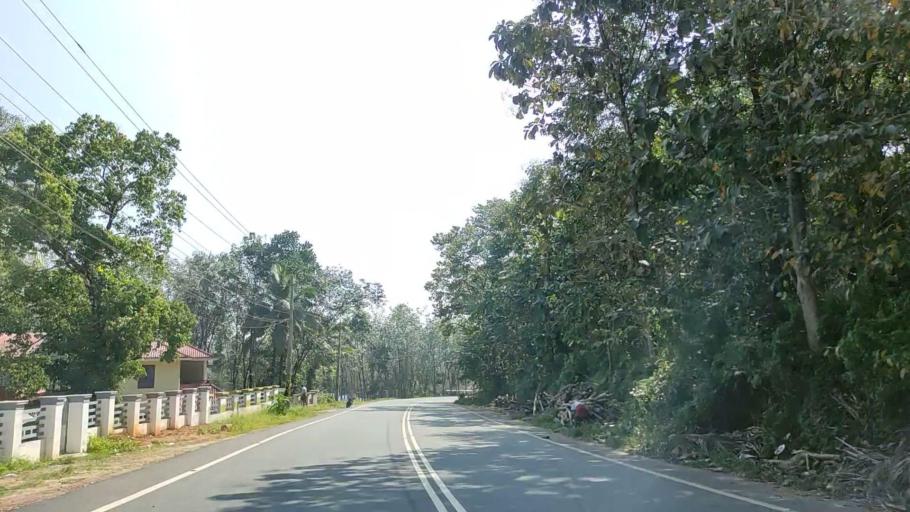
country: IN
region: Kerala
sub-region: Kollam
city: Punalur
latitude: 8.9204
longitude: 77.0368
